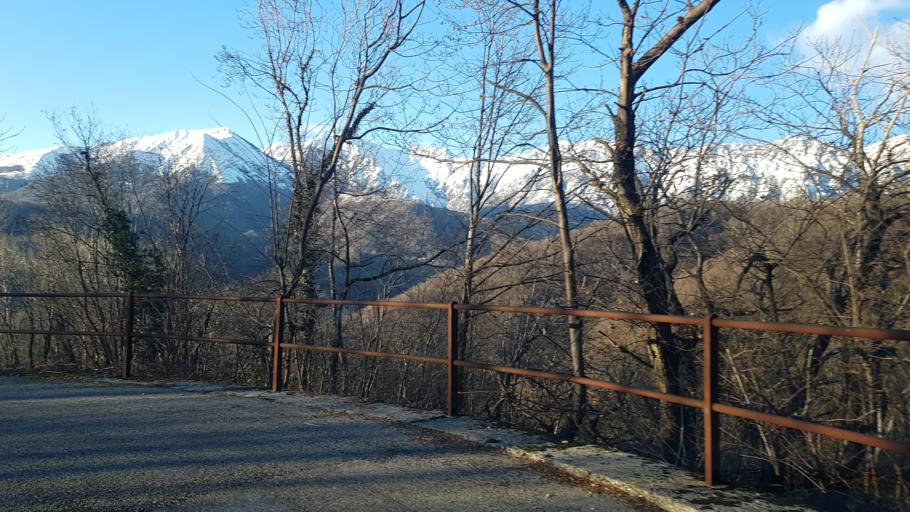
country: IT
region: Friuli Venezia Giulia
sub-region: Provincia di Udine
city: Tarcento
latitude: 46.2482
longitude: 13.2250
